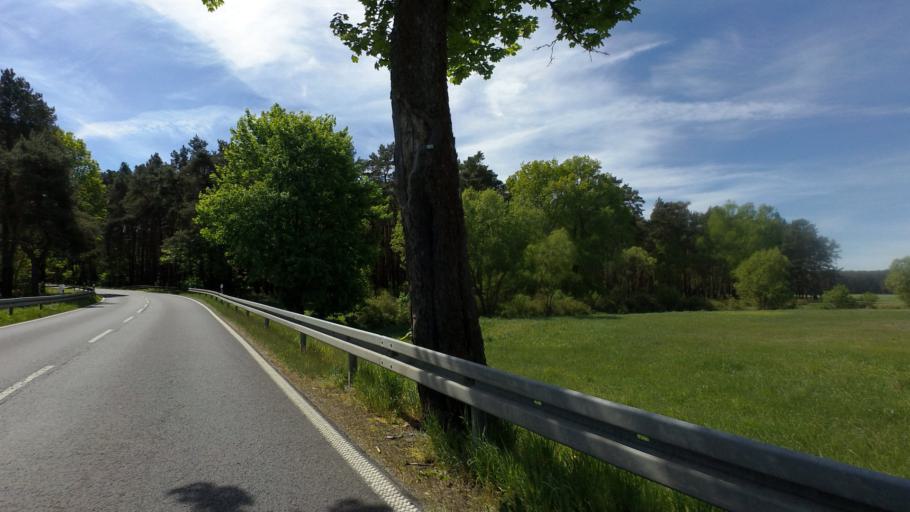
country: DE
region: Brandenburg
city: Luckenwalde
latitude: 52.1342
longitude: 13.1274
